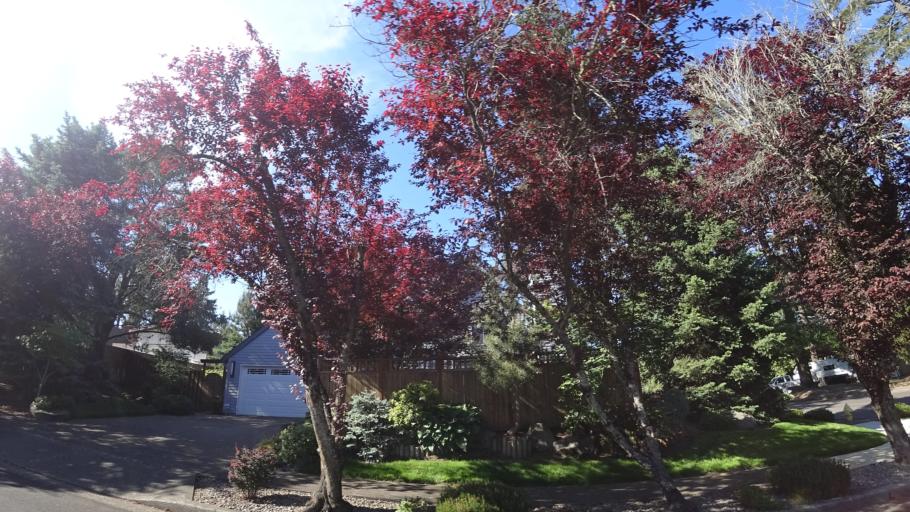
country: US
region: Oregon
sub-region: Washington County
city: Beaverton
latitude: 45.4538
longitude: -122.8109
